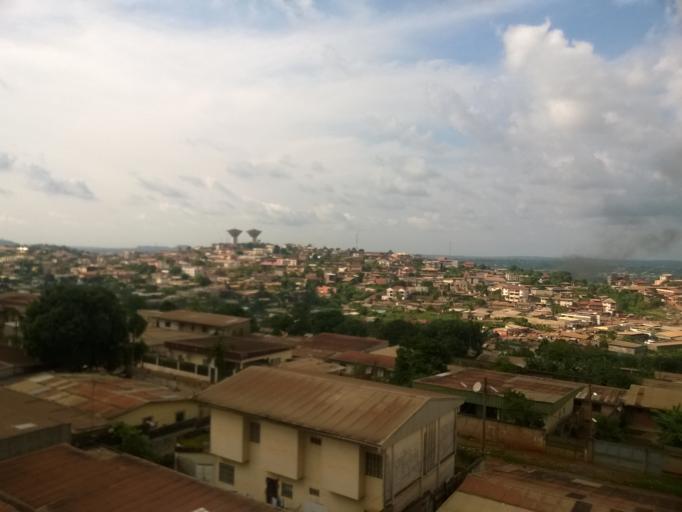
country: CM
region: Centre
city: Yaounde
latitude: 3.9055
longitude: 11.5334
